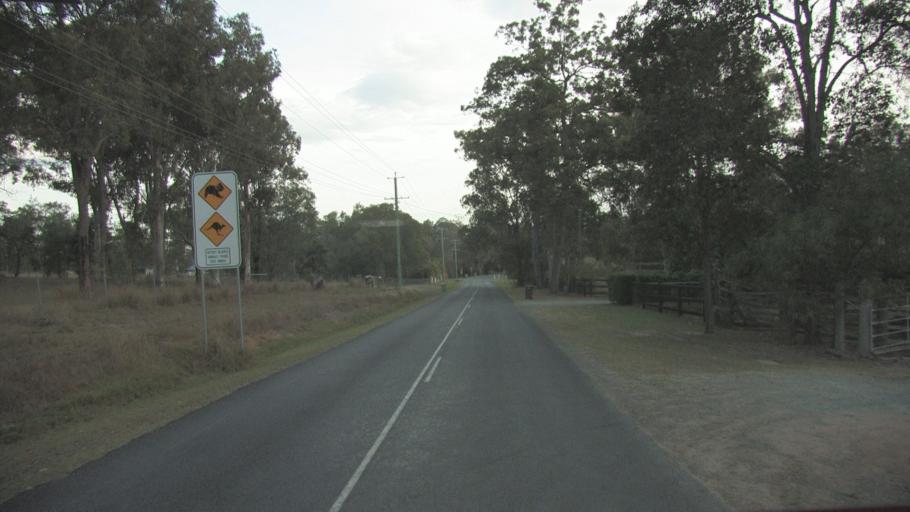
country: AU
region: Queensland
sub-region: Logan
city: Cedar Vale
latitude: -27.8385
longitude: 153.1059
